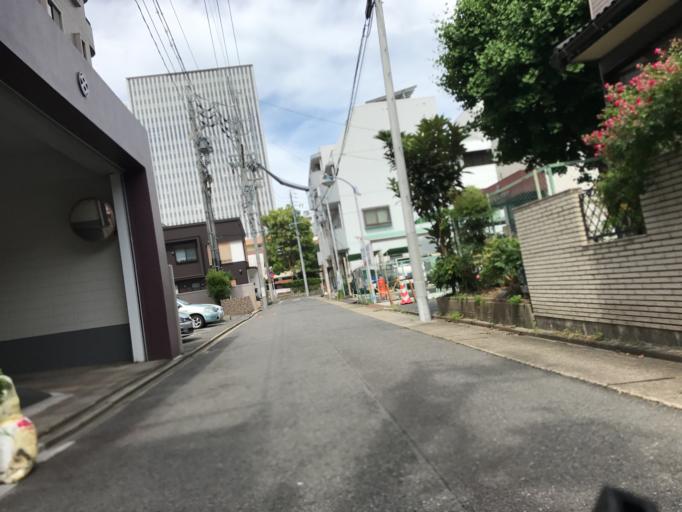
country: JP
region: Aichi
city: Nagoya-shi
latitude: 35.1764
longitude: 136.8885
